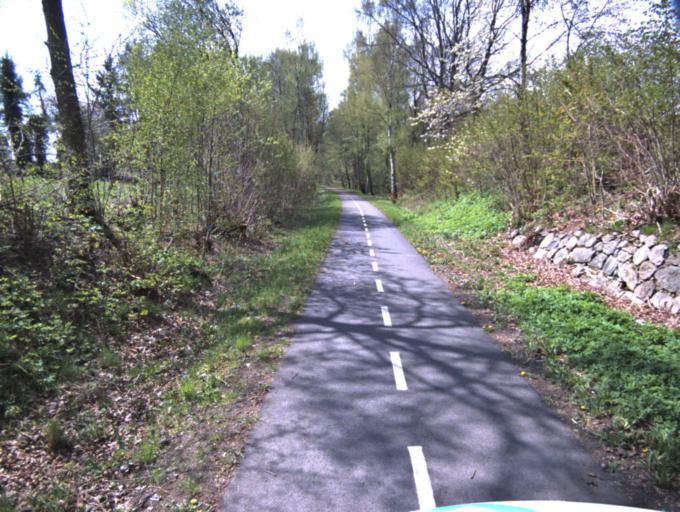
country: SE
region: Skane
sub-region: Kristianstads Kommun
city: Onnestad
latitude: 55.9993
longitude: 14.0422
